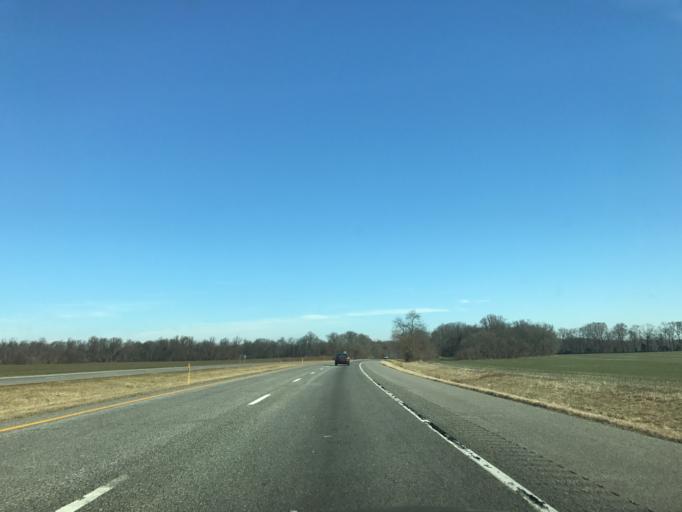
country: US
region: Delaware
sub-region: New Castle County
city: Townsend
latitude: 39.3719
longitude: -75.8129
